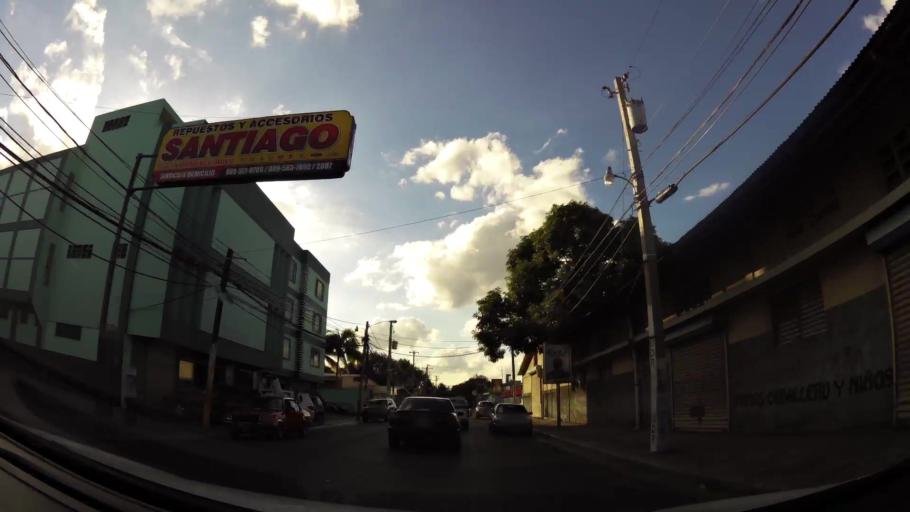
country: DO
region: Santiago
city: Santiago de los Caballeros
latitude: 19.4597
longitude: -70.7007
